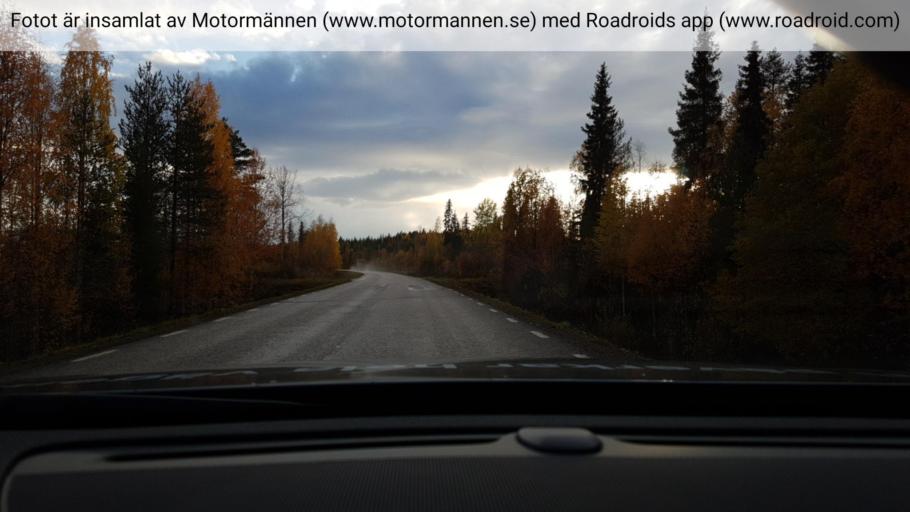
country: SE
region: Norrbotten
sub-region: Overkalix Kommun
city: OEverkalix
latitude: 66.7826
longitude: 22.7069
